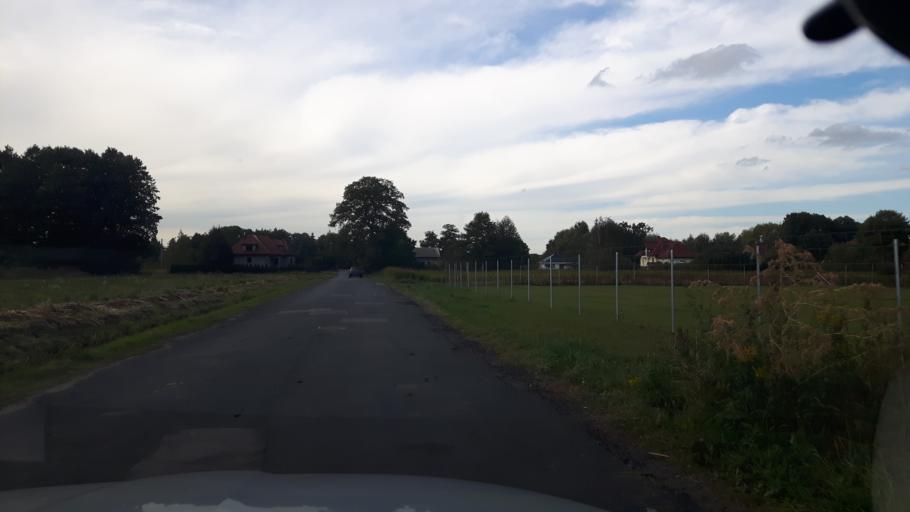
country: PL
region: Masovian Voivodeship
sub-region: Powiat legionowski
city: Stanislawow Pierwszy
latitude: 52.3506
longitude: 21.0593
